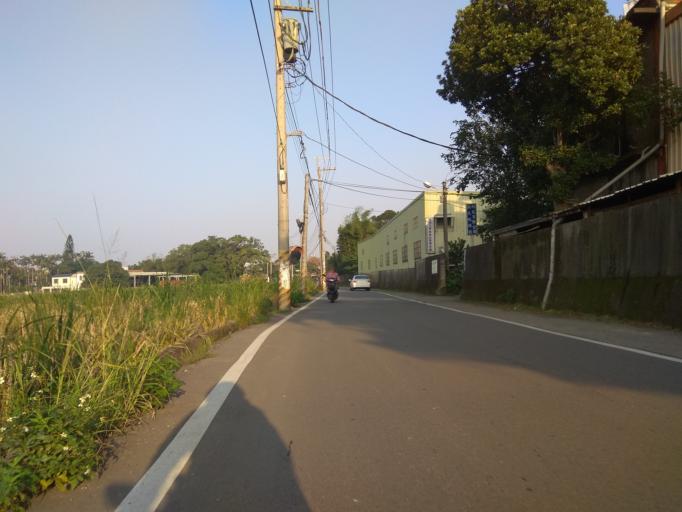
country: TW
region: Taiwan
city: Daxi
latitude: 24.9077
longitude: 121.1934
